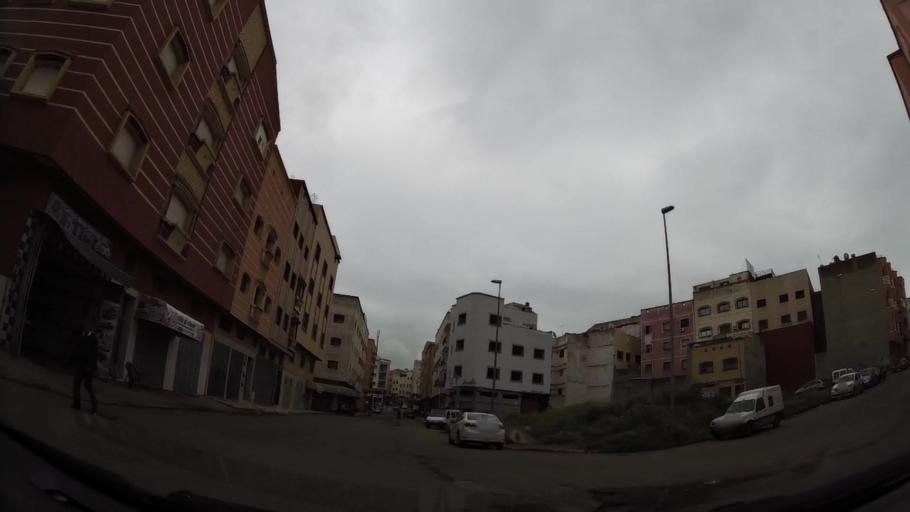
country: MA
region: Grand Casablanca
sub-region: Casablanca
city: Casablanca
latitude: 33.5326
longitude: -7.6104
